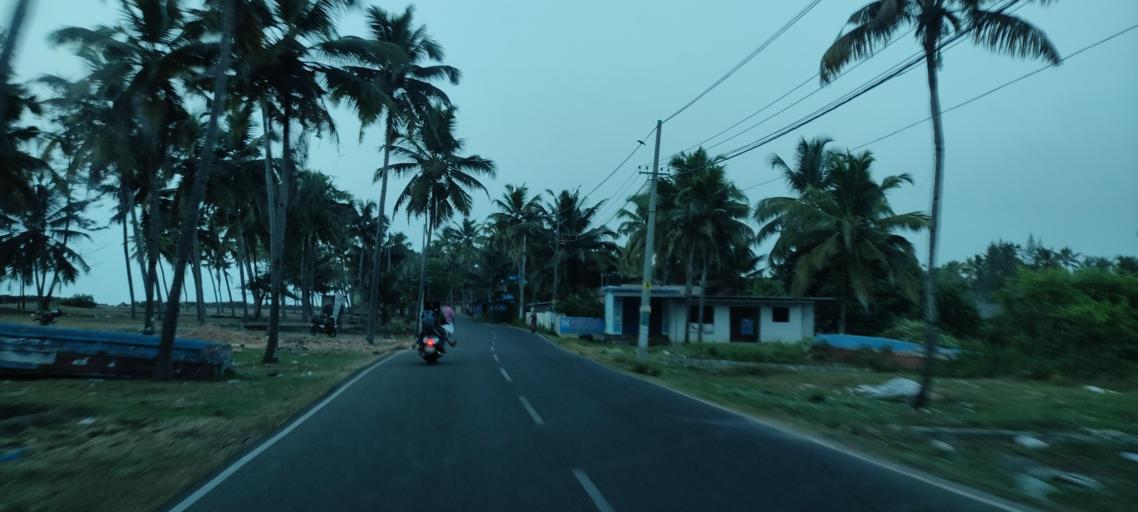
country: IN
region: Kerala
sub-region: Alappuzha
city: Kayankulam
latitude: 9.1214
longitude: 76.4704
